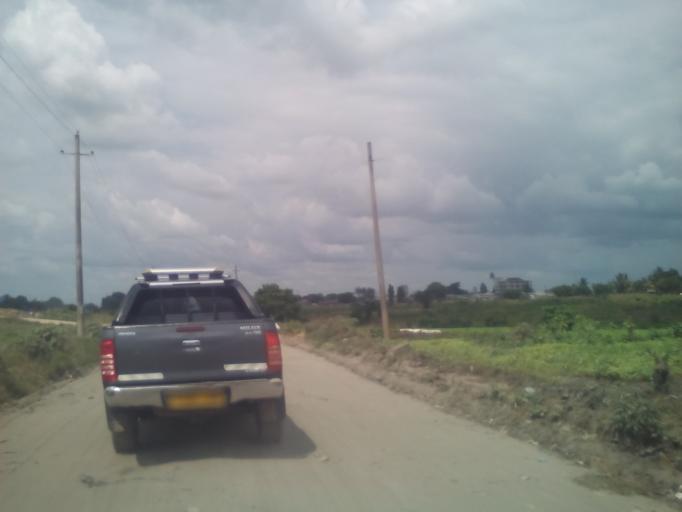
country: TZ
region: Dar es Salaam
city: Dar es Salaam
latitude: -6.8561
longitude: 39.2424
